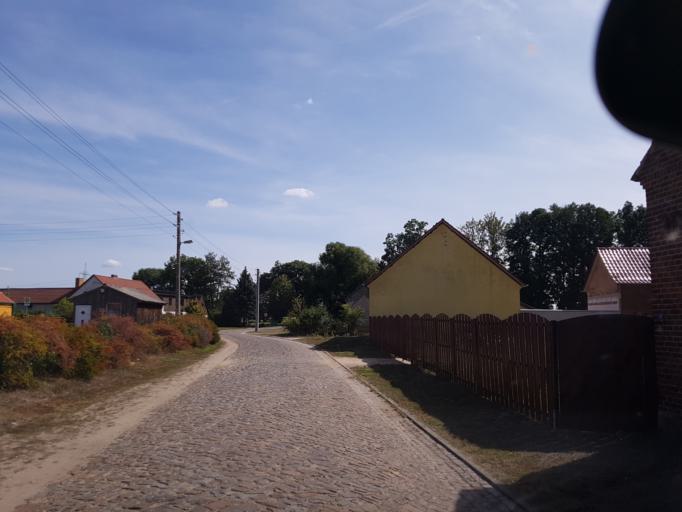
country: DE
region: Brandenburg
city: Luckau
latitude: 51.8646
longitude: 13.6474
